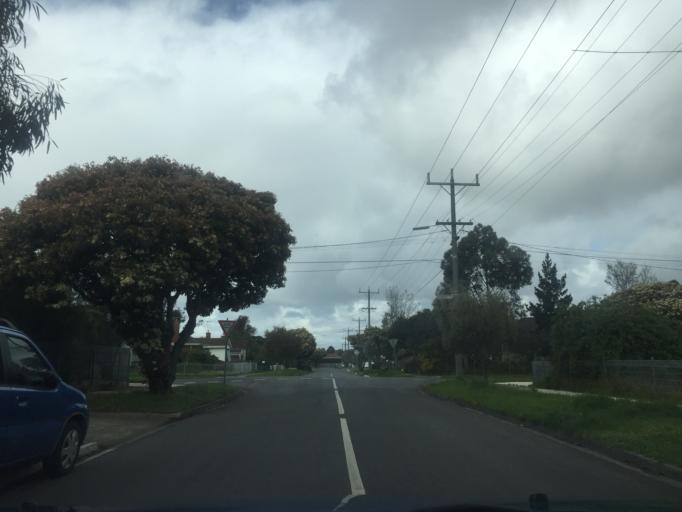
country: AU
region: Victoria
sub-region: Banyule
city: Bellfield
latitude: -37.7509
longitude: 145.0373
